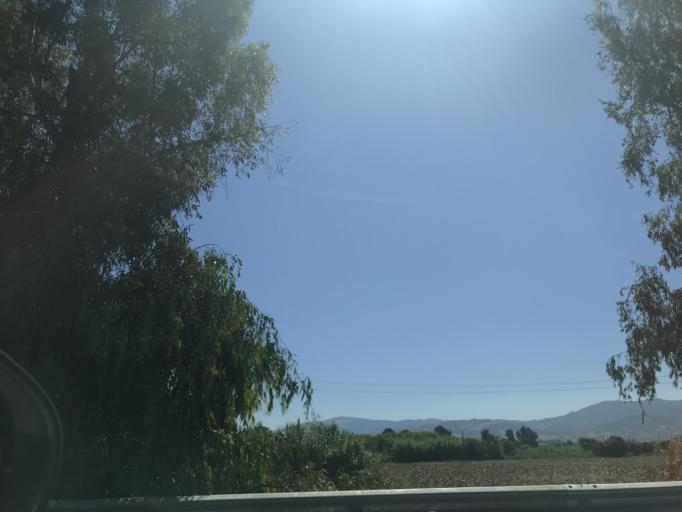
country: TR
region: Aydin
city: Aydin
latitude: 37.8182
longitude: 27.8466
